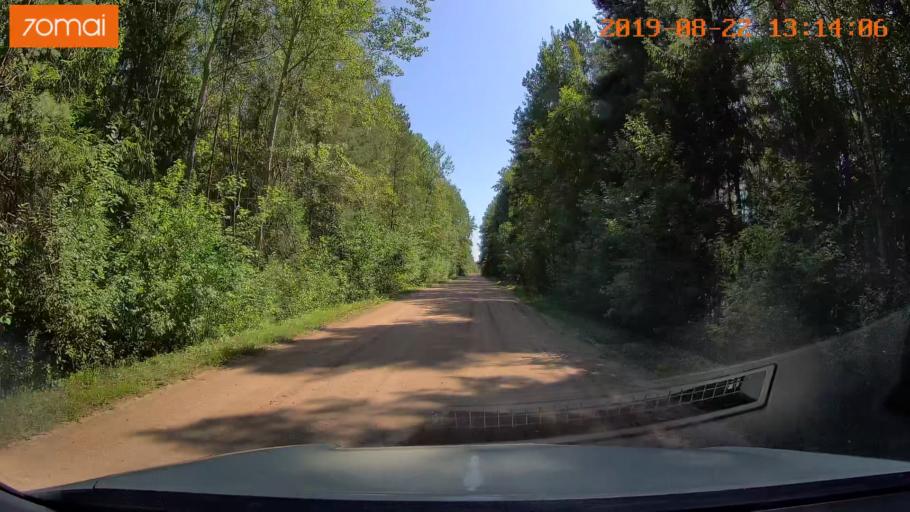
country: BY
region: Minsk
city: Prawdzinski
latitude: 53.2709
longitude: 27.8834
